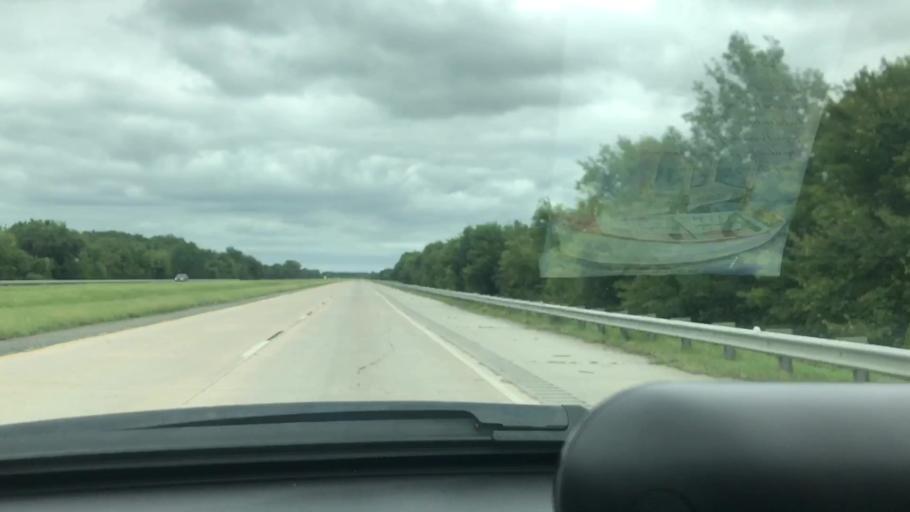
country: US
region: Oklahoma
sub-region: Wagoner County
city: Wagoner
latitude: 35.8922
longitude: -95.4026
